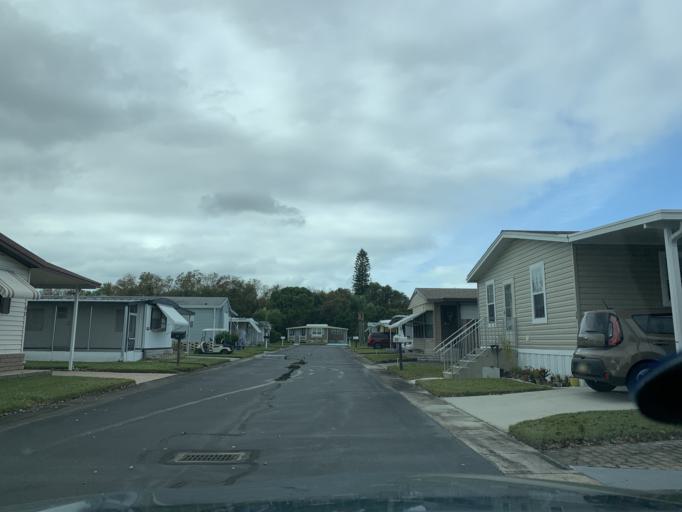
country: US
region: Florida
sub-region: Pinellas County
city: Ridgecrest
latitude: 27.8866
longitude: -82.7921
